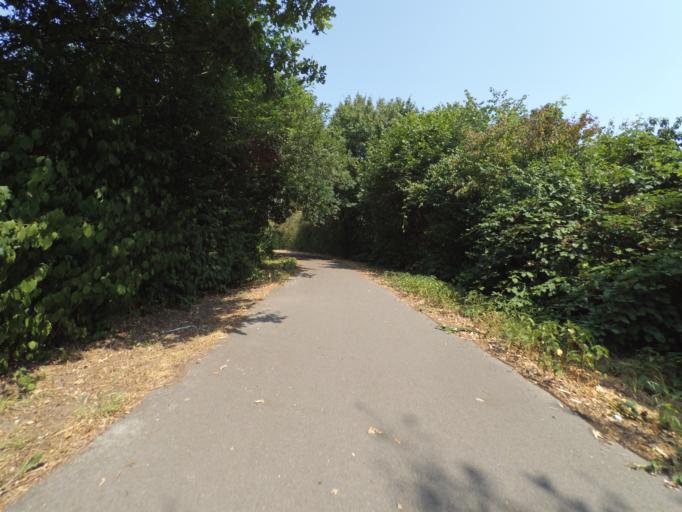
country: DE
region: North Rhine-Westphalia
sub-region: Regierungsbezirk Dusseldorf
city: Mehrhoog
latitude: 51.7296
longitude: 6.4690
